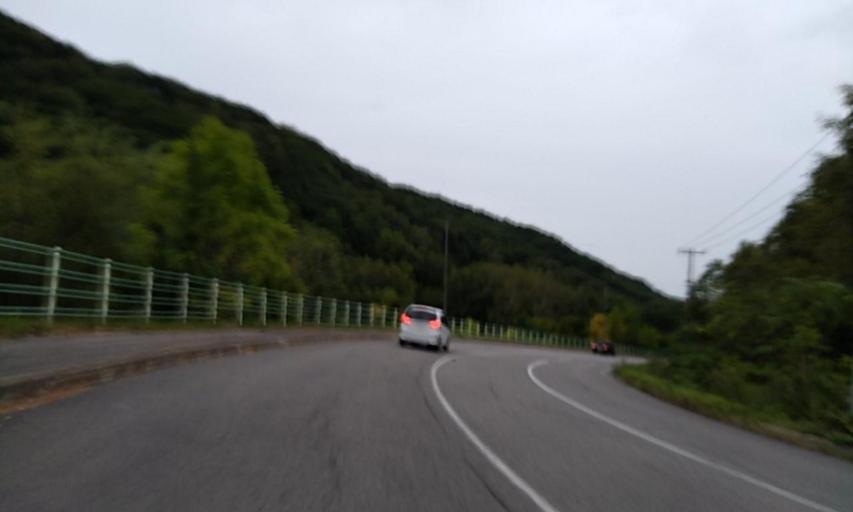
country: JP
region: Hokkaido
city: Abashiri
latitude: 43.9978
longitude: 144.2290
